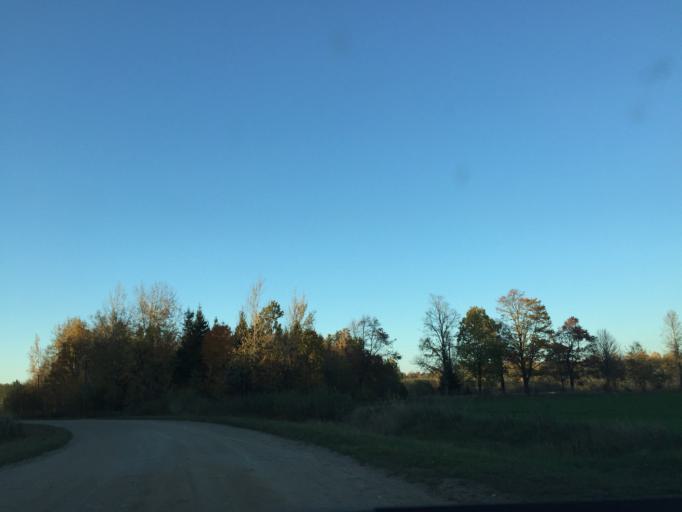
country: LT
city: Vieksniai
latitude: 56.3397
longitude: 22.5451
